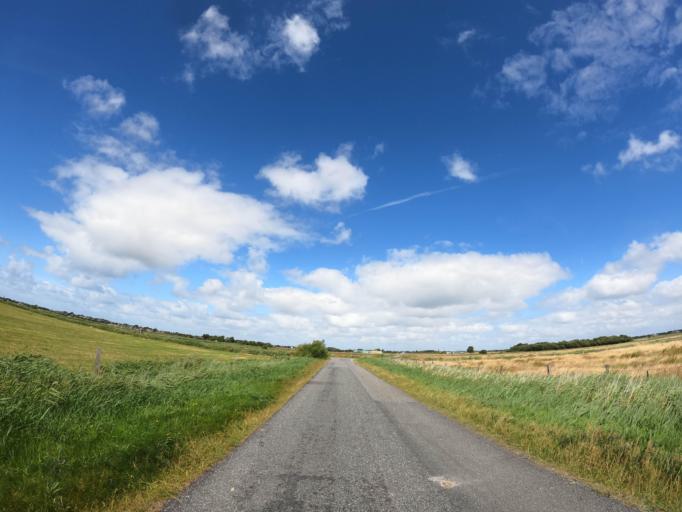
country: DE
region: Schleswig-Holstein
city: Tinnum
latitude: 54.8867
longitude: 8.3423
